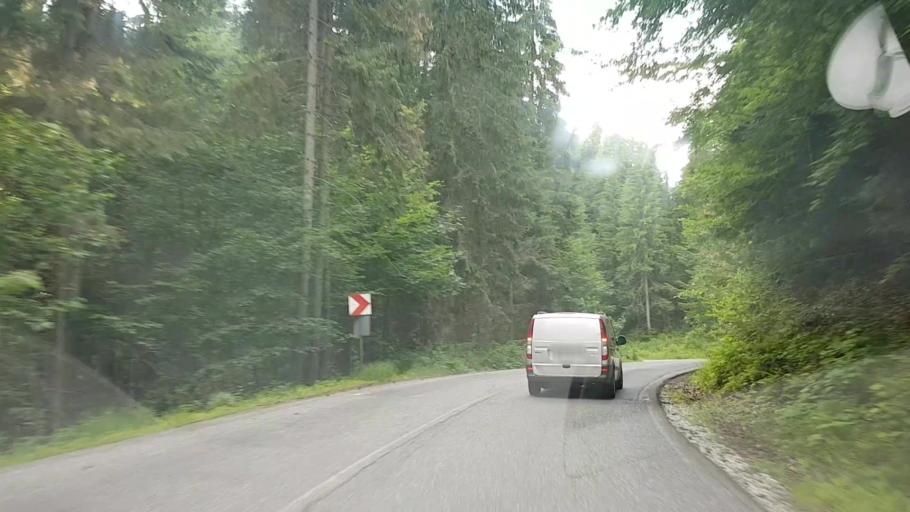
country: RO
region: Harghita
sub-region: Comuna Remetea
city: Remetea
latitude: 46.6727
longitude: 25.3499
